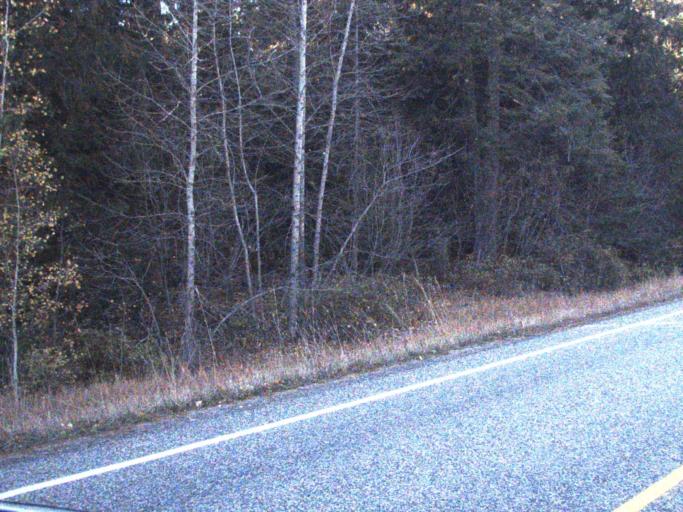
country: CA
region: British Columbia
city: Rossland
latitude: 48.9896
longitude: -117.8288
